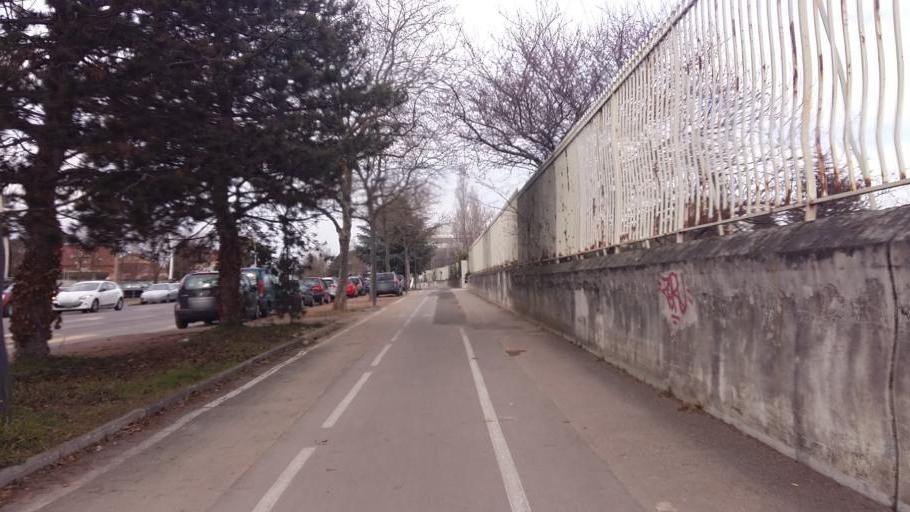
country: FR
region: Rhone-Alpes
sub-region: Departement du Rhone
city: Bron
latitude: 45.7461
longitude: 4.8963
